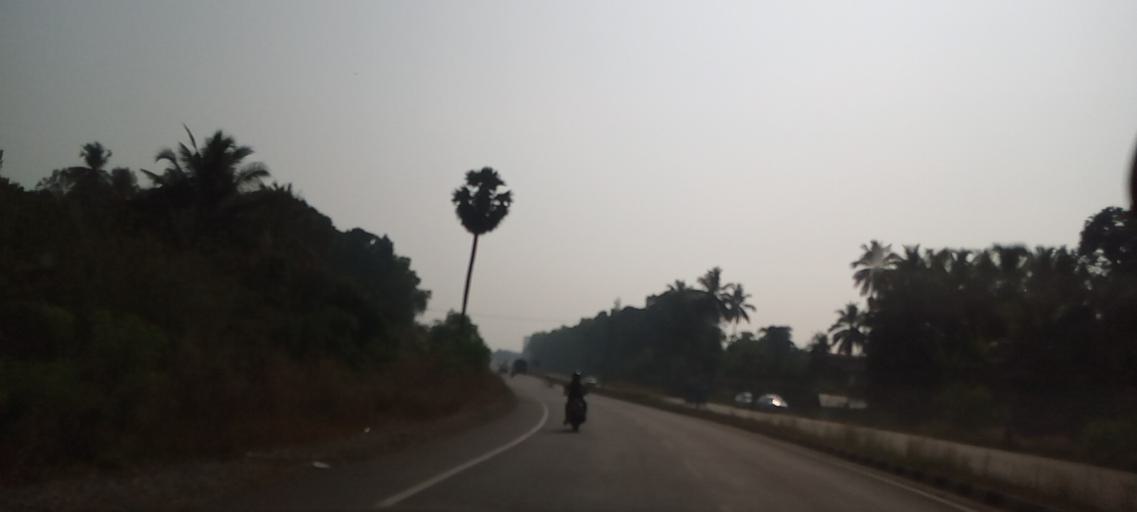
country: IN
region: Karnataka
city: Gangolli
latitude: 13.6782
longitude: 74.6893
